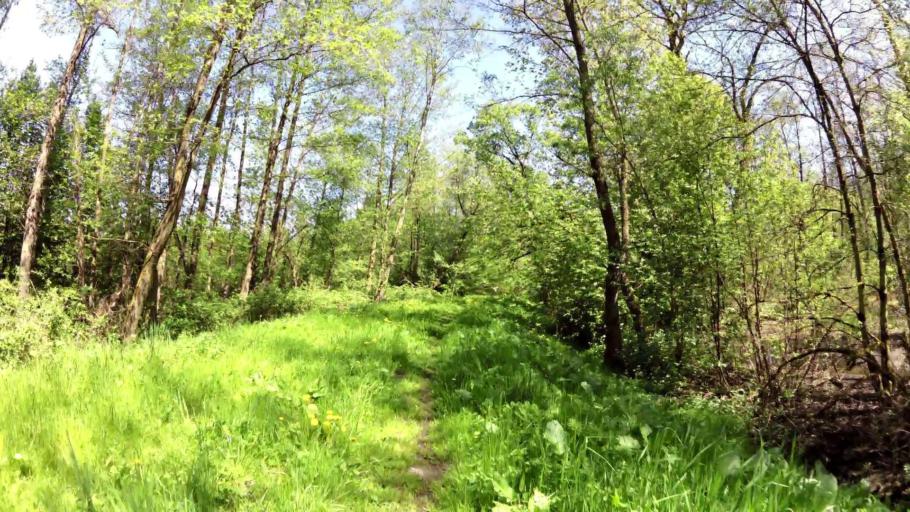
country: PL
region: West Pomeranian Voivodeship
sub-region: Powiat bialogardzki
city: Bialogard
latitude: 53.9983
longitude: 16.0269
